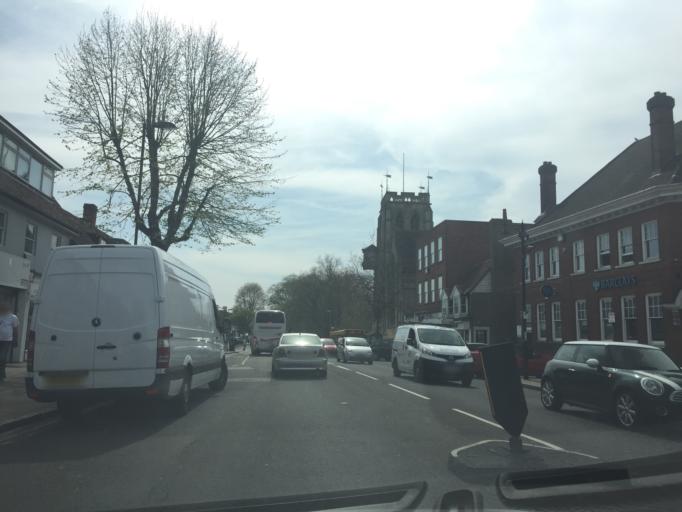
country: GB
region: England
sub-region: Essex
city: Epping
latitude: 51.6991
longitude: 0.1116
